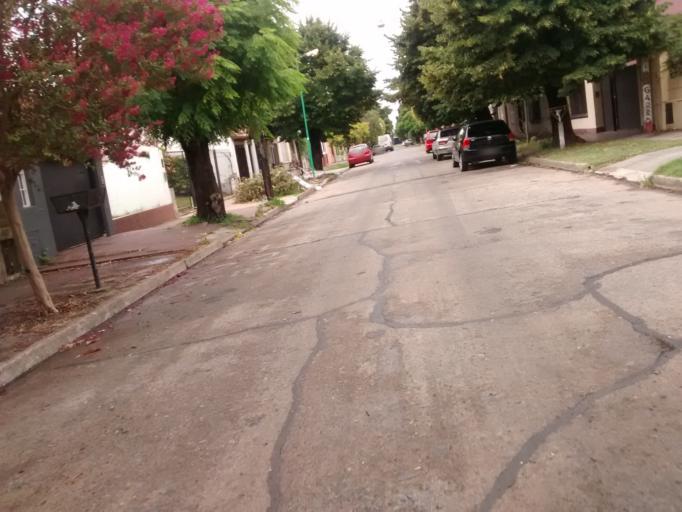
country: AR
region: Buenos Aires
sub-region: Partido de La Plata
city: La Plata
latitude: -34.8950
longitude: -57.9678
